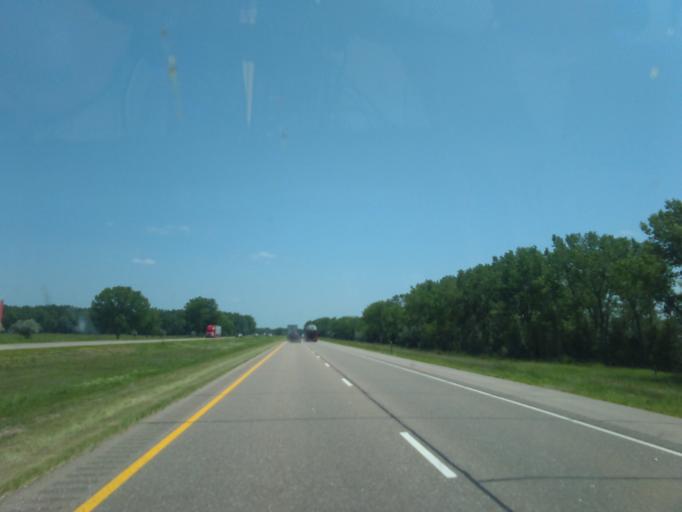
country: US
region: Nebraska
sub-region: Dawson County
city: Gothenburg
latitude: 40.8914
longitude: -100.1092
